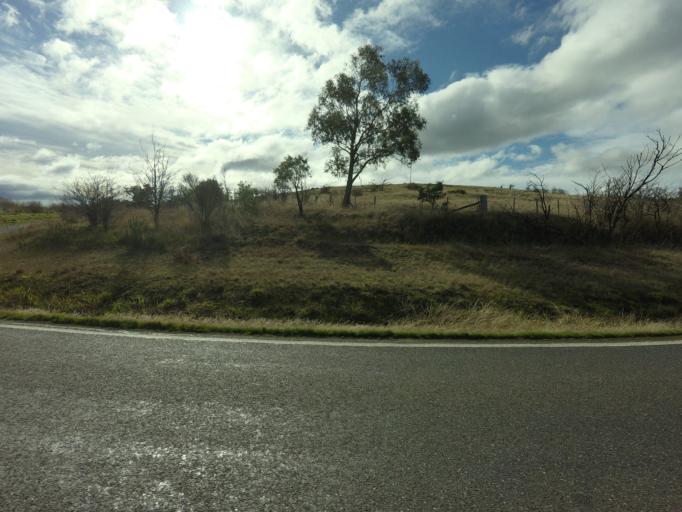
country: AU
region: Tasmania
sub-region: Derwent Valley
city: New Norfolk
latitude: -42.6519
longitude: 146.9327
